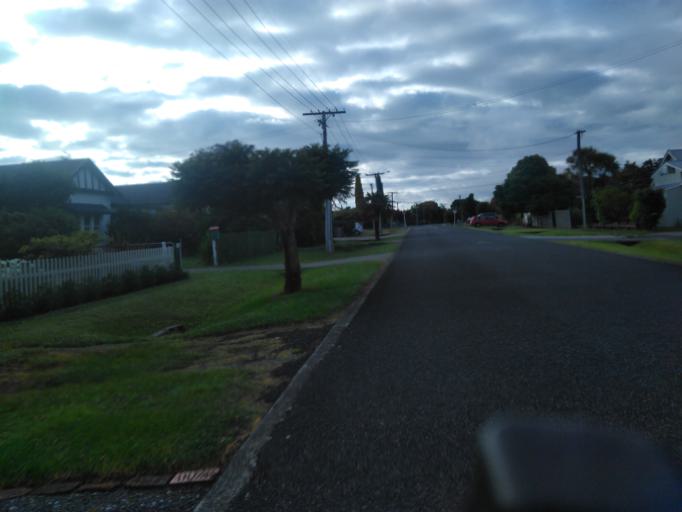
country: NZ
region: Gisborne
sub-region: Gisborne District
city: Gisborne
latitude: -38.6566
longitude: 178.0287
